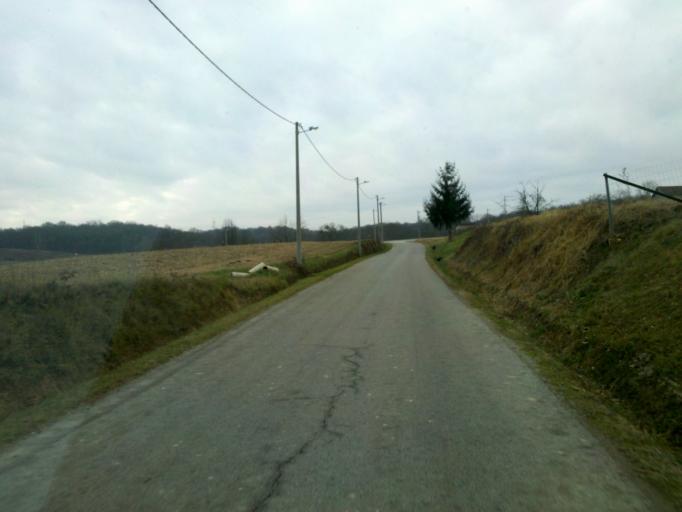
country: HR
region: Grad Zagreb
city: Horvati
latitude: 45.6852
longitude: 15.8479
